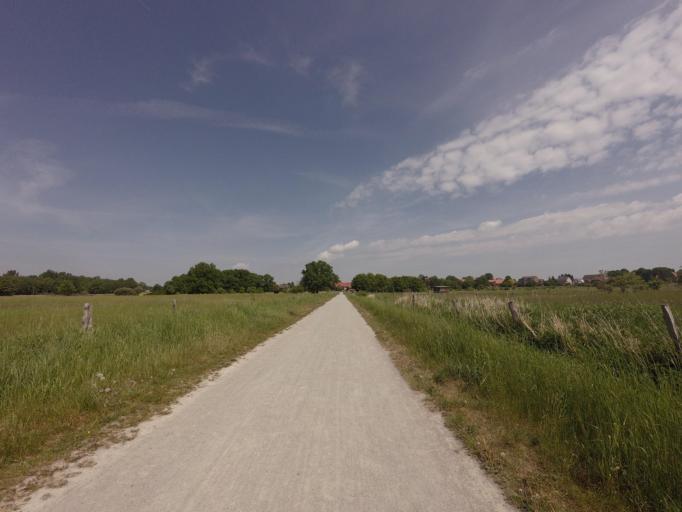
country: DE
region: Lower Saxony
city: Cremlingen
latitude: 52.2740
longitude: 10.6028
